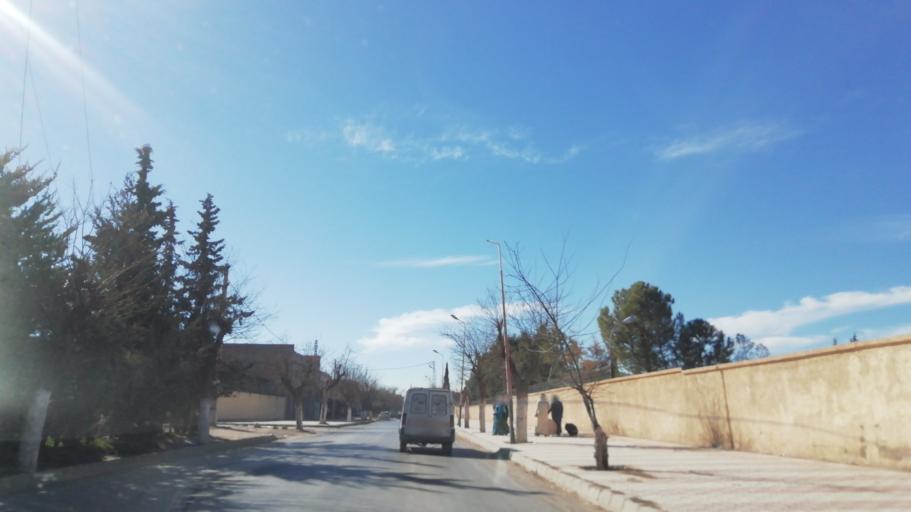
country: DZ
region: Tlemcen
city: Sebdou
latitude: 34.6502
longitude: -1.3197
